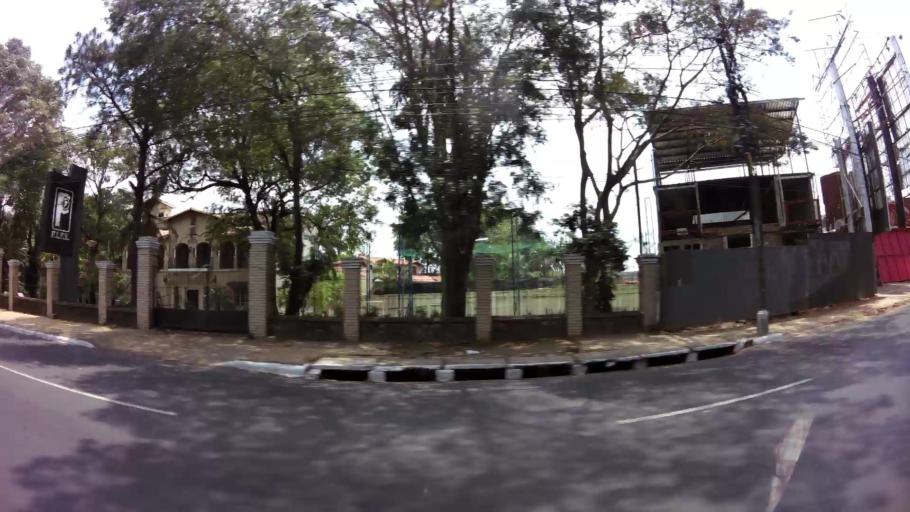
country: PY
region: Asuncion
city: Asuncion
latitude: -25.2933
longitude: -57.6080
